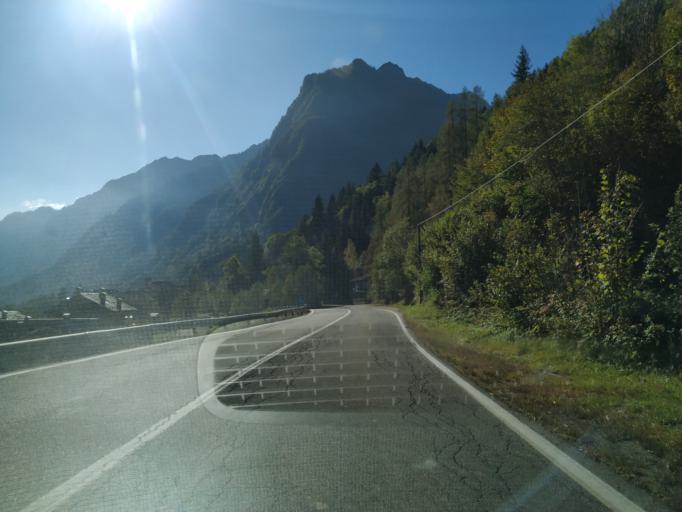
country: IT
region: Piedmont
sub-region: Provincia di Vercelli
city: Riva Valdobbia
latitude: 45.8378
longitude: 7.9477
